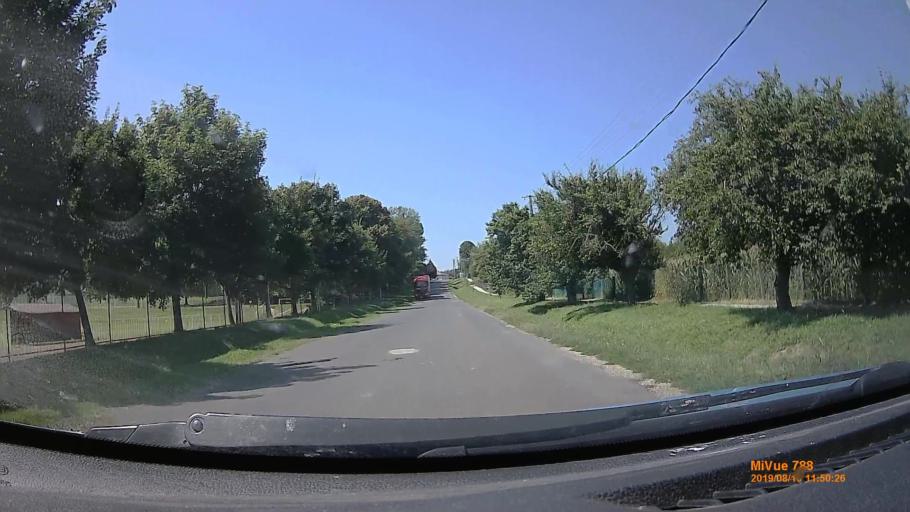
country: HU
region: Somogy
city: Somogyvar
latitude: 46.4929
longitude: 17.7191
